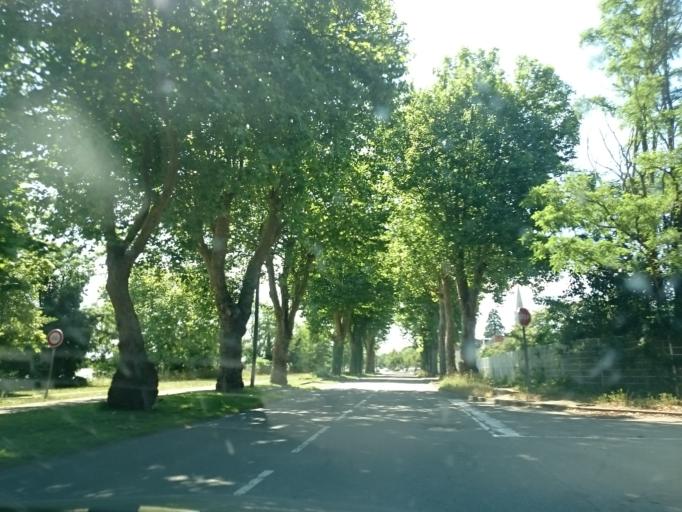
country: FR
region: Pays de la Loire
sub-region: Departement de la Loire-Atlantique
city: Coueron
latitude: 47.2088
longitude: -1.7232
